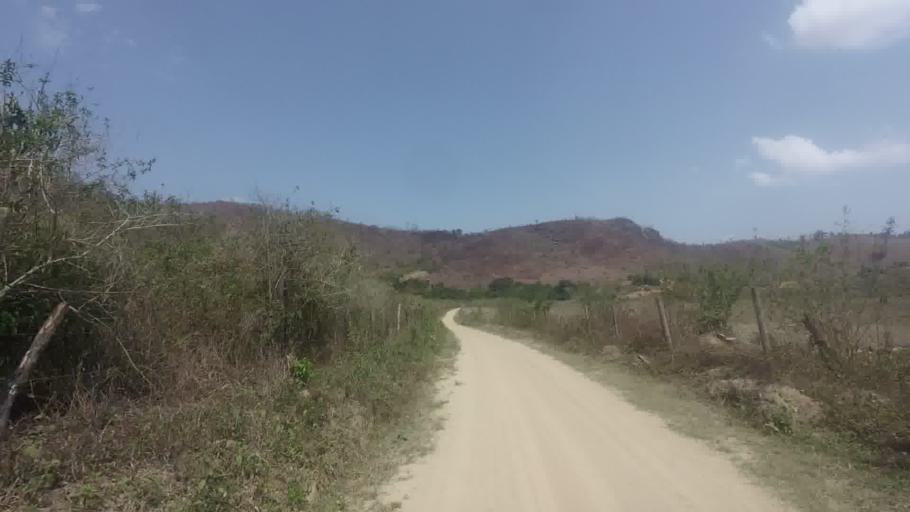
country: BR
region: Espirito Santo
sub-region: Sao Jose Do Calcado
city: Sao Jose do Calcado
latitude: -21.0250
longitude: -41.5181
